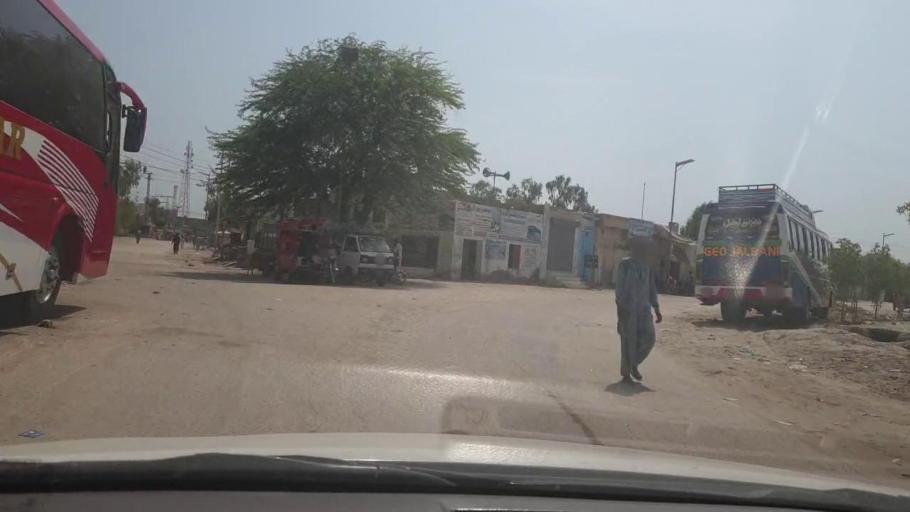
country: PK
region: Sindh
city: Garhi Yasin
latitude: 27.9099
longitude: 68.5148
